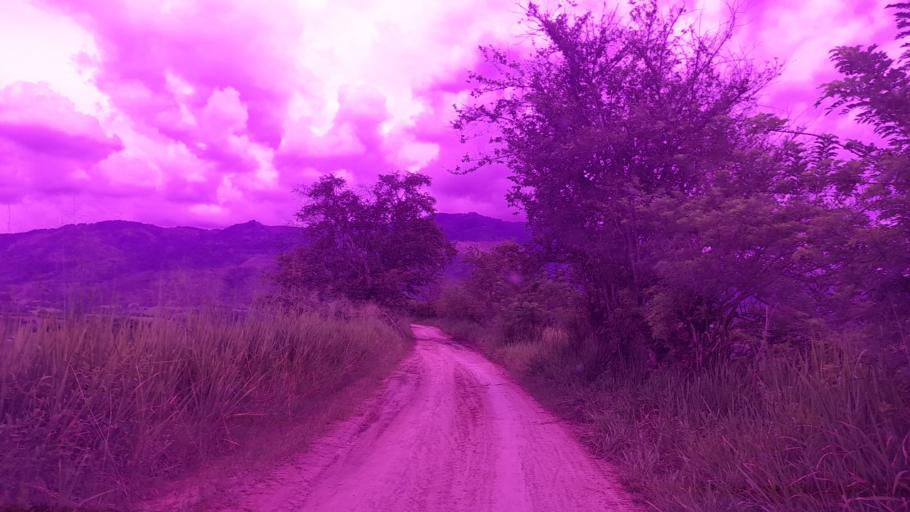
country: CO
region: Valle del Cauca
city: Andalucia
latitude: 4.1722
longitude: -76.0961
